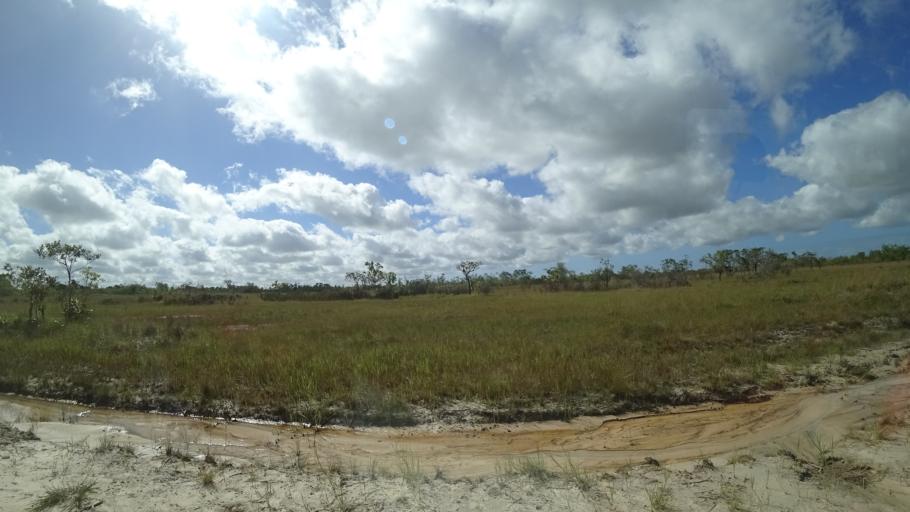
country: MZ
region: Sofala
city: Dondo
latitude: -19.5777
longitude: 35.0870
